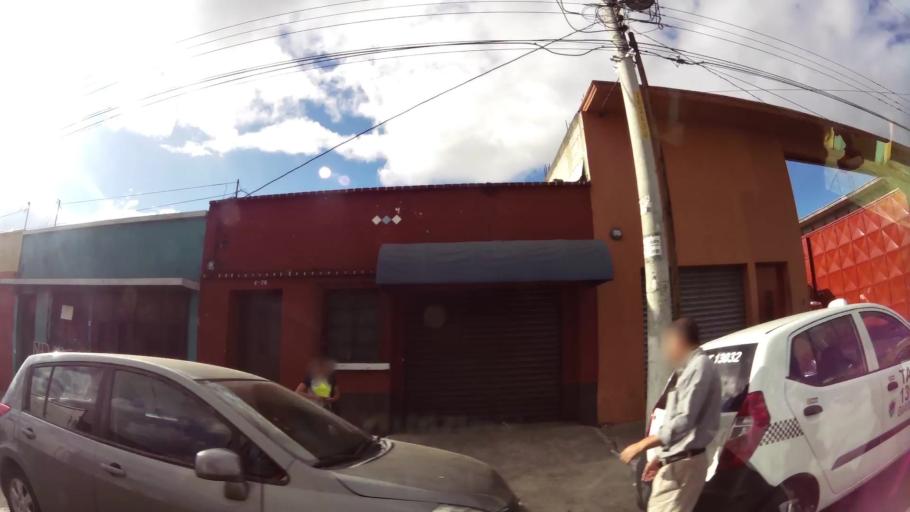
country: GT
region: Guatemala
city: Guatemala City
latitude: 14.6184
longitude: -90.5474
